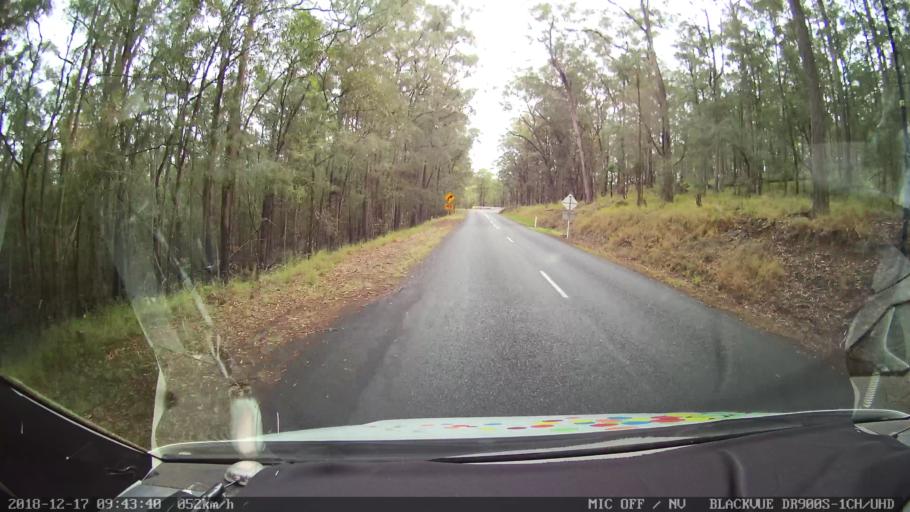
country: AU
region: New South Wales
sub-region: Tenterfield Municipality
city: Carrolls Creek
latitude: -28.9236
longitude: 152.3220
